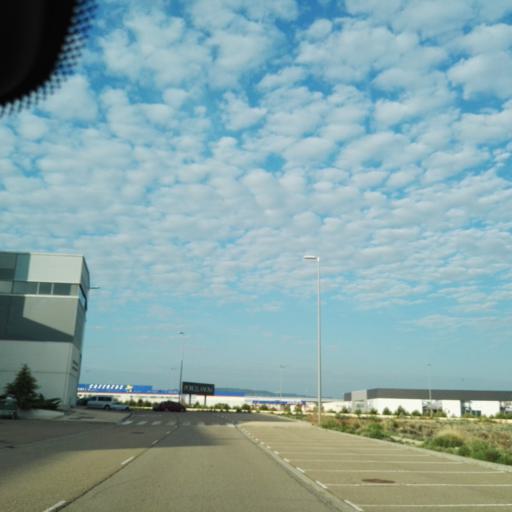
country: ES
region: Aragon
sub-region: Provincia de Zaragoza
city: Montecanal
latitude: 41.6492
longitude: -0.9961
